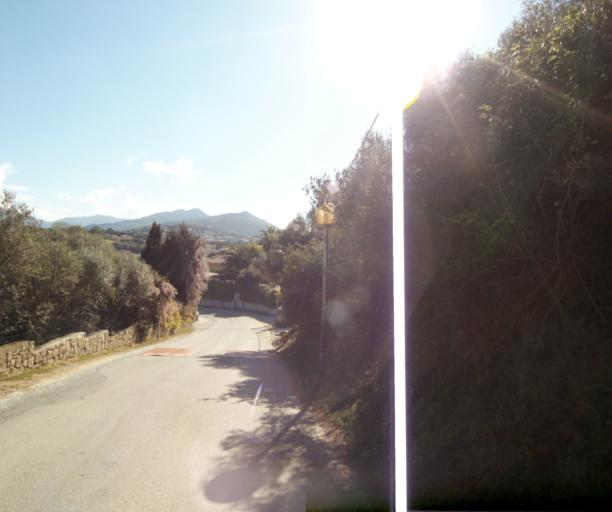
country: FR
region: Corsica
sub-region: Departement de la Corse-du-Sud
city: Propriano
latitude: 41.6710
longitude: 8.9067
